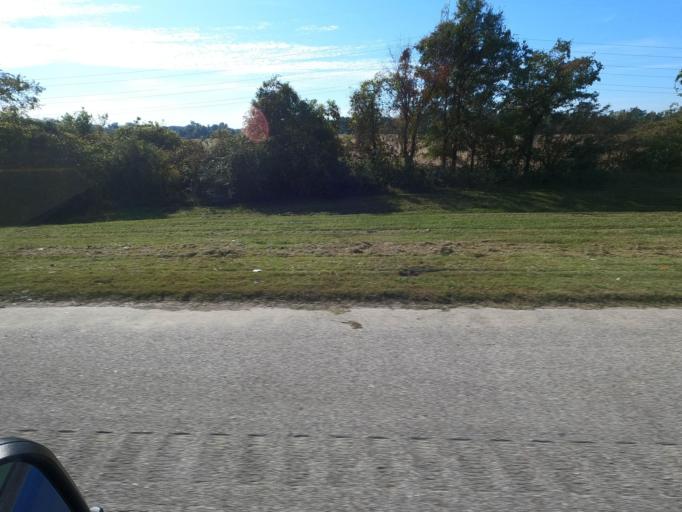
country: US
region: Tennessee
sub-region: Shelby County
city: Millington
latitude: 35.3303
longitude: -89.9104
